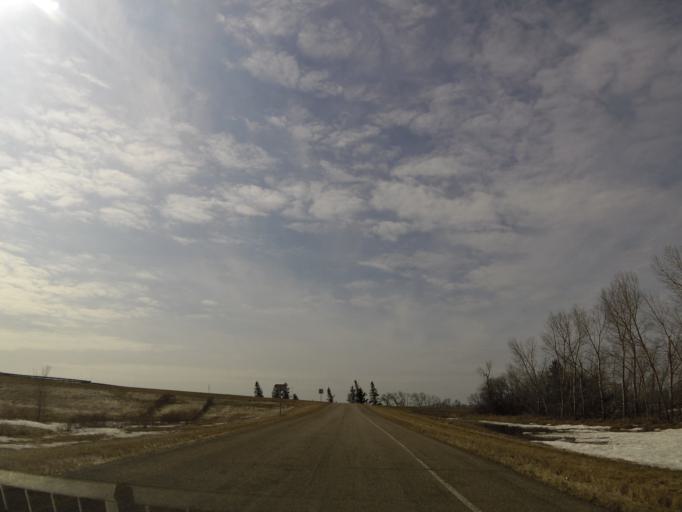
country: US
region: North Dakota
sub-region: Walsh County
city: Grafton
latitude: 48.3546
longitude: -97.1904
